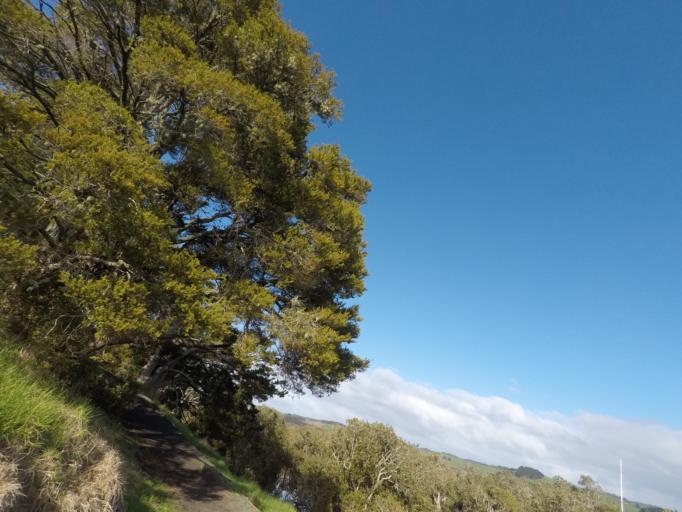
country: NZ
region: Auckland
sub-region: Auckland
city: Warkworth
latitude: -36.4296
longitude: 174.7183
